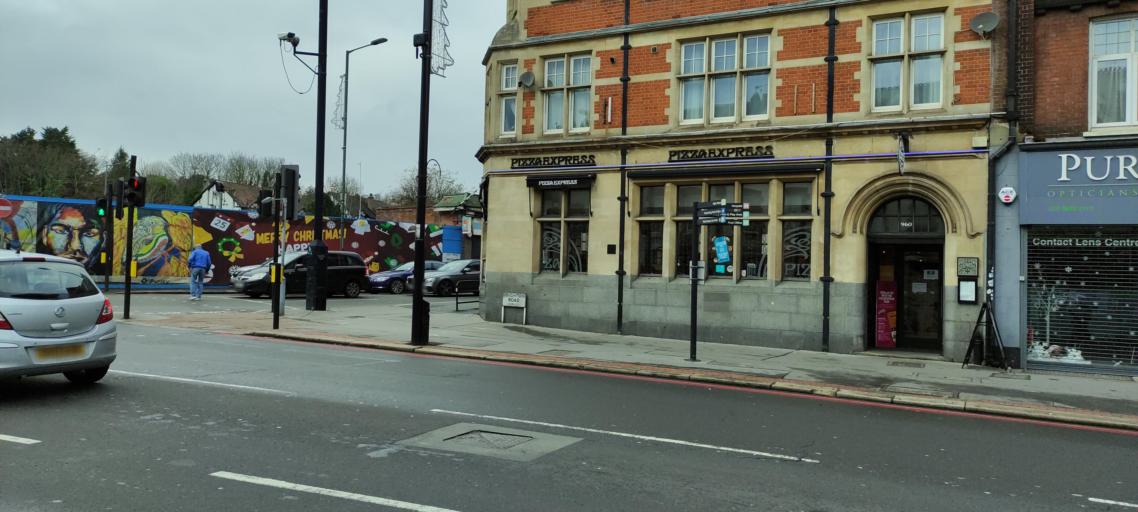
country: GB
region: England
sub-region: Greater London
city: Purley
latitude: 51.3387
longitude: -0.1165
